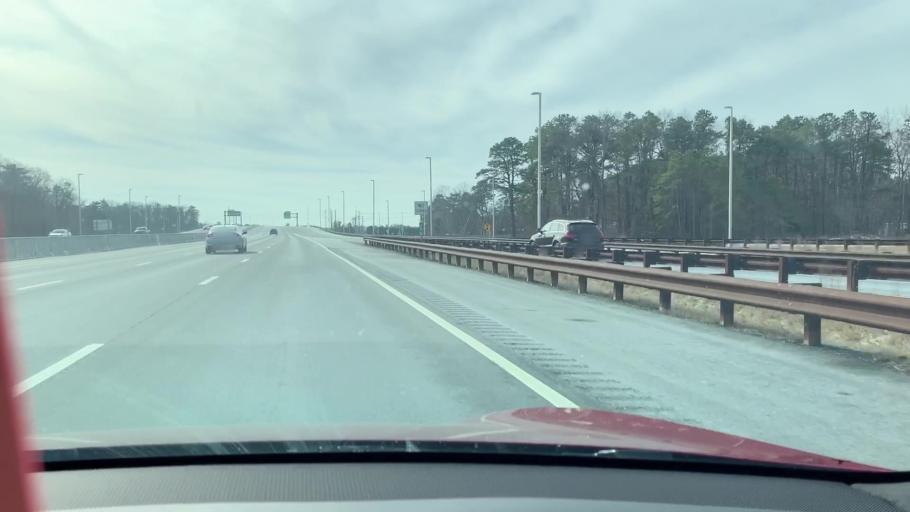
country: US
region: New Jersey
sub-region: Atlantic County
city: Pleasantville
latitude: 39.4084
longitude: -74.5561
